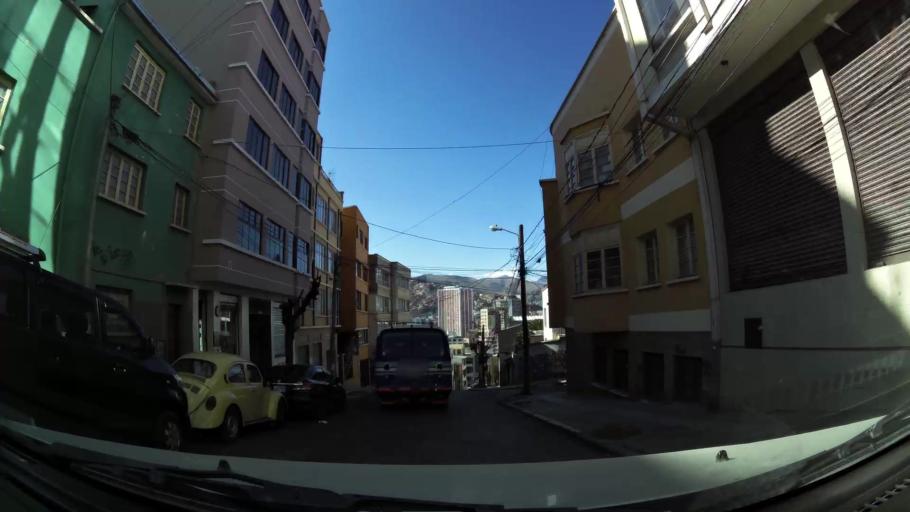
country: BO
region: La Paz
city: La Paz
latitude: -16.5065
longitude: -68.1340
